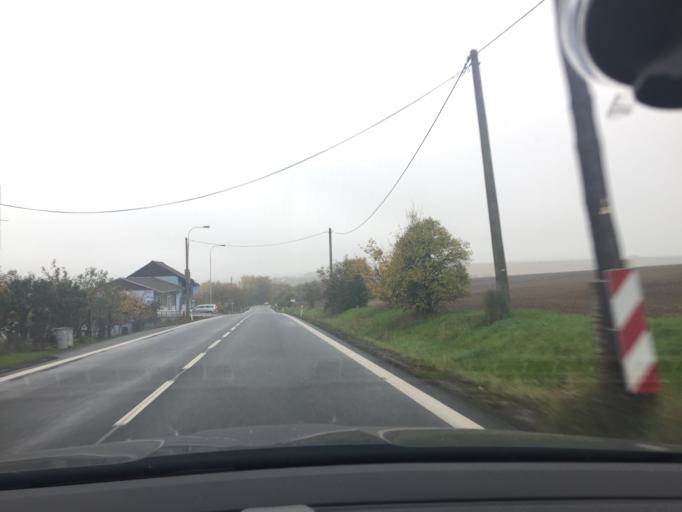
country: CZ
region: South Moravian
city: Rousinov
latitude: 49.1968
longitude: 16.8649
